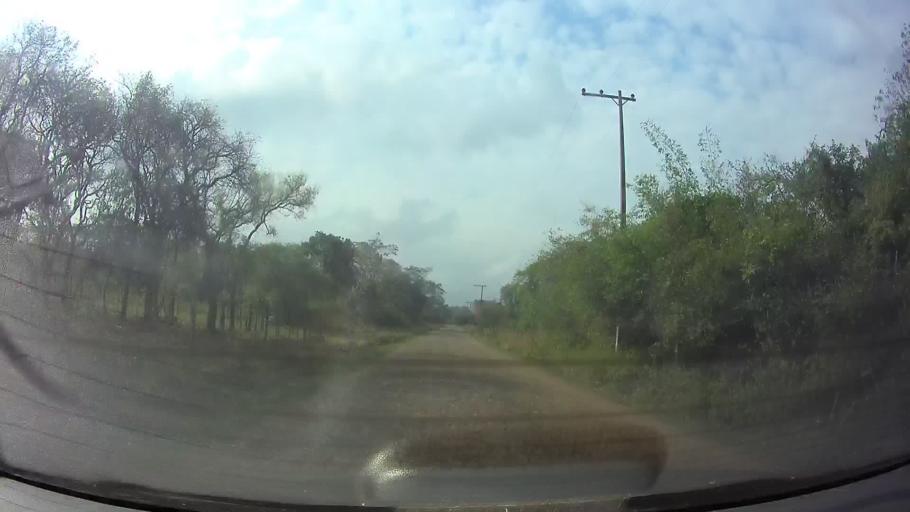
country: PY
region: Cordillera
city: Arroyos y Esteros
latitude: -24.9945
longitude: -57.1935
